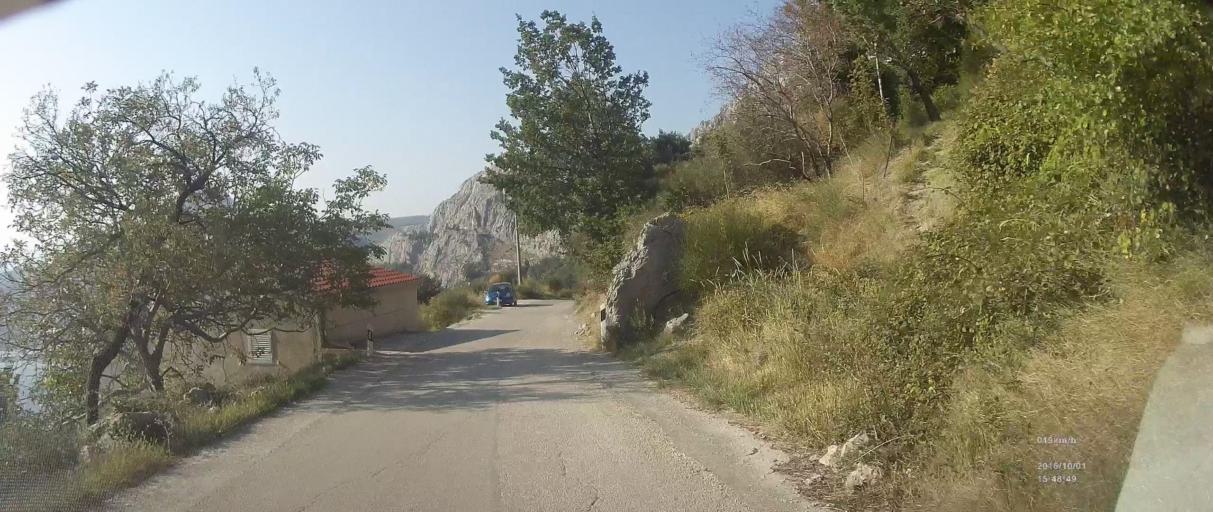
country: HR
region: Splitsko-Dalmatinska
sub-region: Grad Omis
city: Omis
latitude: 43.4382
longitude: 16.7077
